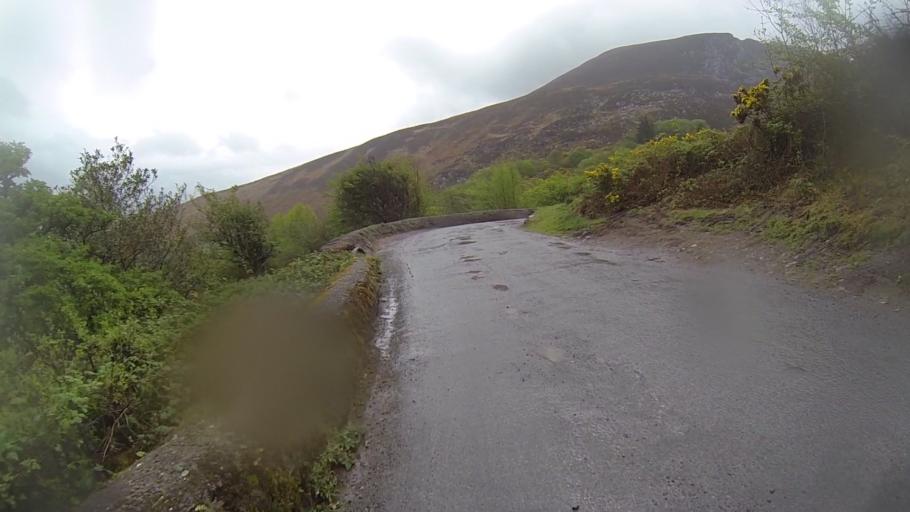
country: IE
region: Munster
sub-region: Ciarrai
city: Cill Airne
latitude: 52.0376
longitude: -9.6360
